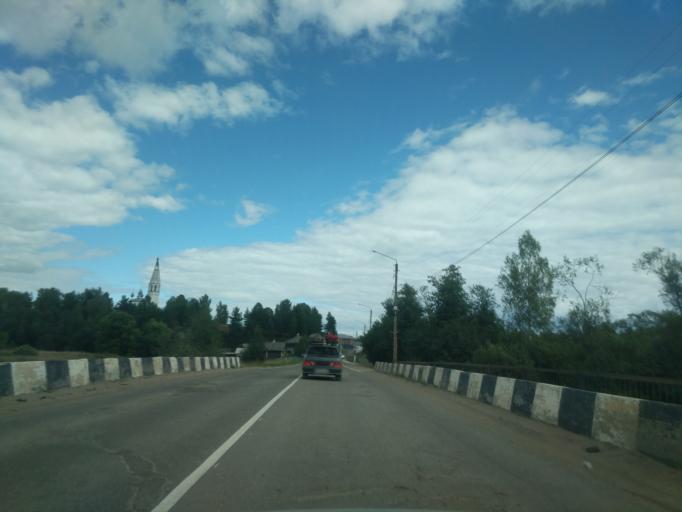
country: RU
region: Kostroma
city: Sudislavl'
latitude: 57.8810
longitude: 41.6992
